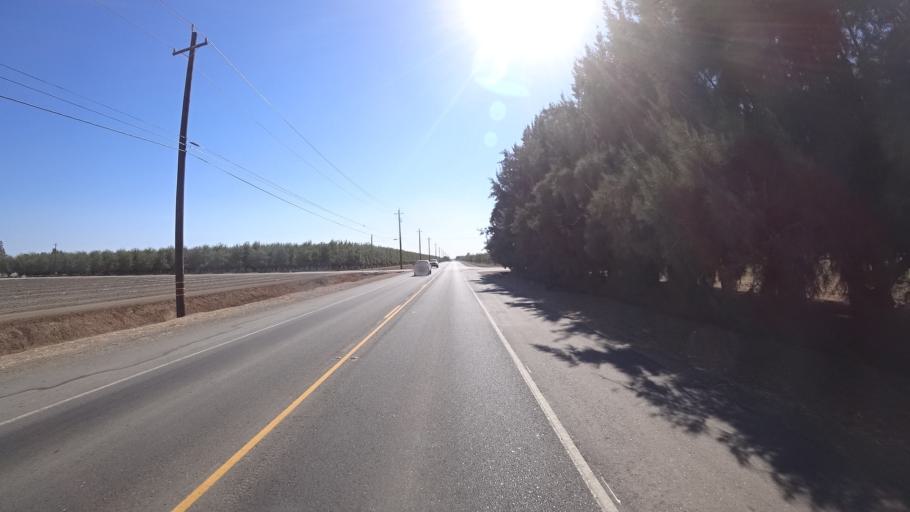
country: US
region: California
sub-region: Yolo County
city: Woodland
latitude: 38.6067
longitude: -121.8030
